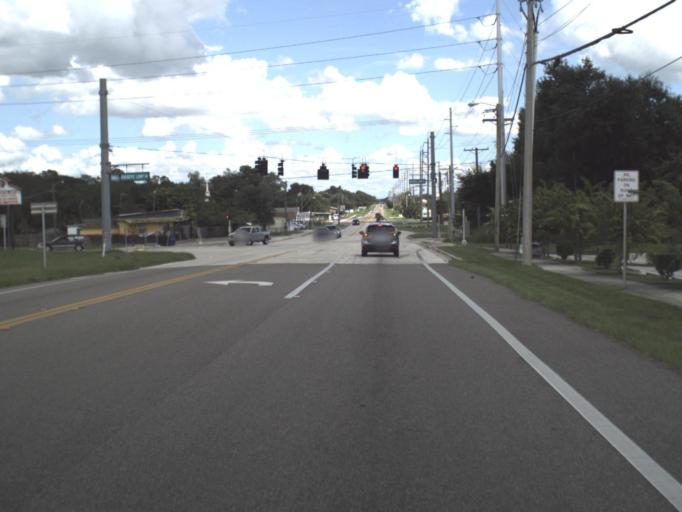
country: US
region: Florida
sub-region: Polk County
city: Cypress Gardens
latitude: 28.0225
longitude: -81.6947
